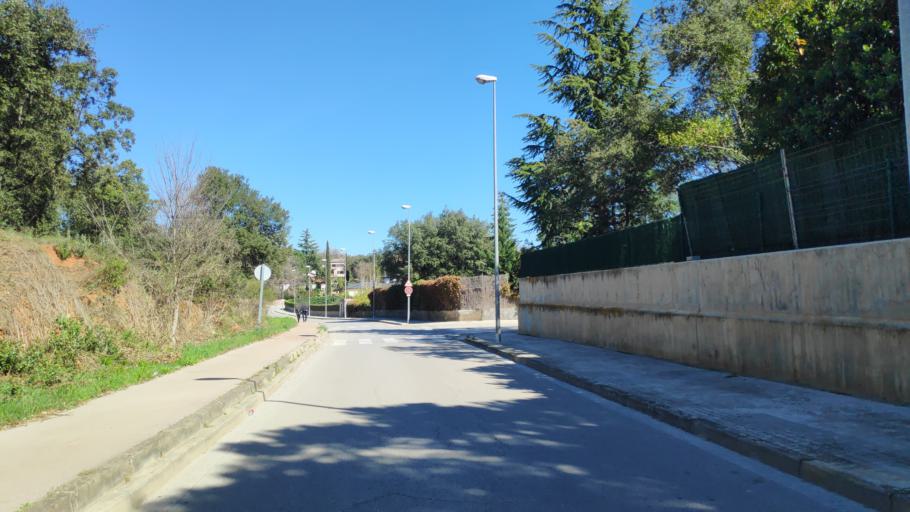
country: ES
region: Catalonia
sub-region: Provincia de Barcelona
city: Sant Quirze del Valles
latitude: 41.5590
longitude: 2.0691
